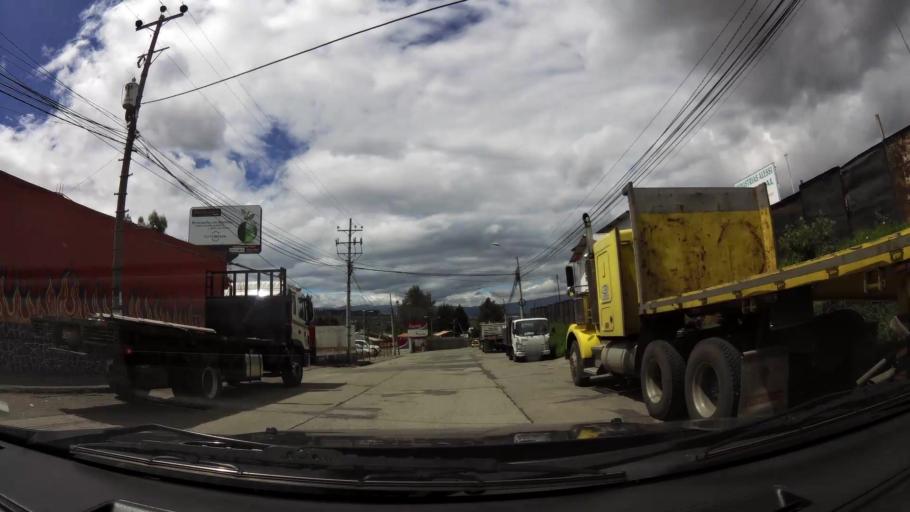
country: EC
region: Pichincha
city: Sangolqui
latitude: -0.3455
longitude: -78.5474
